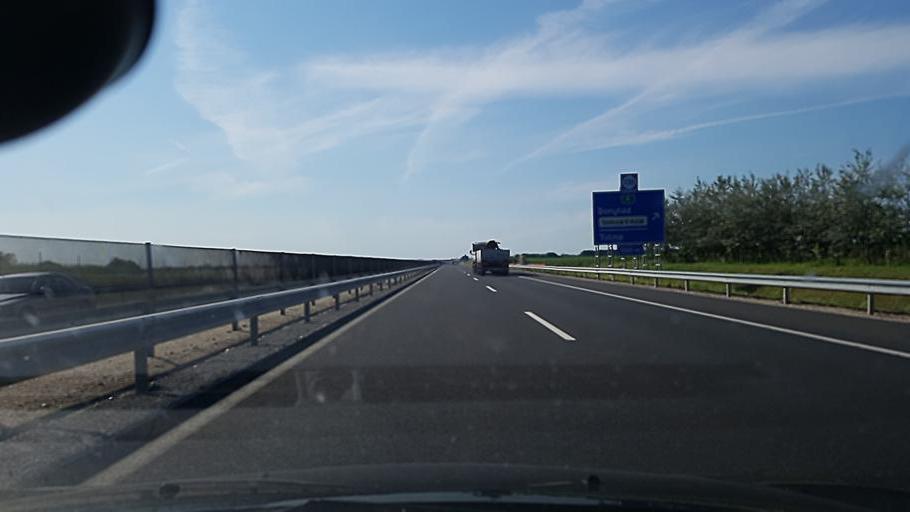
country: HU
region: Tolna
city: Tolna
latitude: 46.4266
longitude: 18.7219
